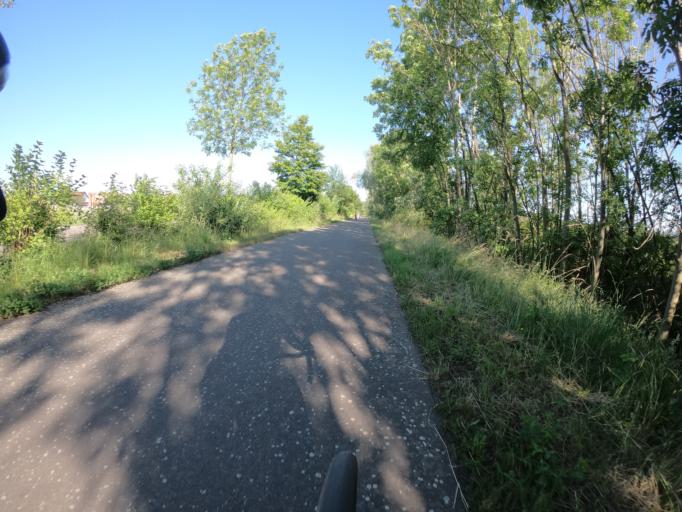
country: DE
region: Brandenburg
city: Juterbog
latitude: 52.0083
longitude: 13.1298
